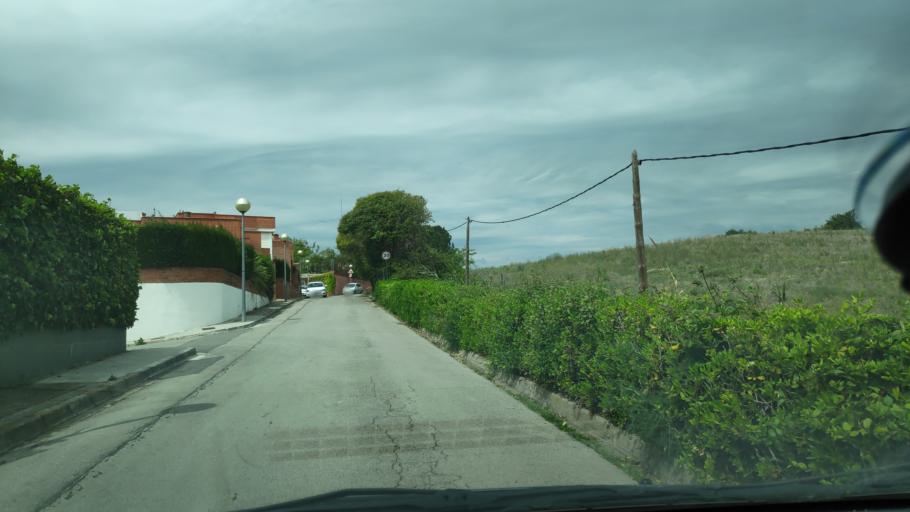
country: ES
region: Catalonia
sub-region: Provincia de Barcelona
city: Barbera del Valles
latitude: 41.5090
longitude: 2.1014
